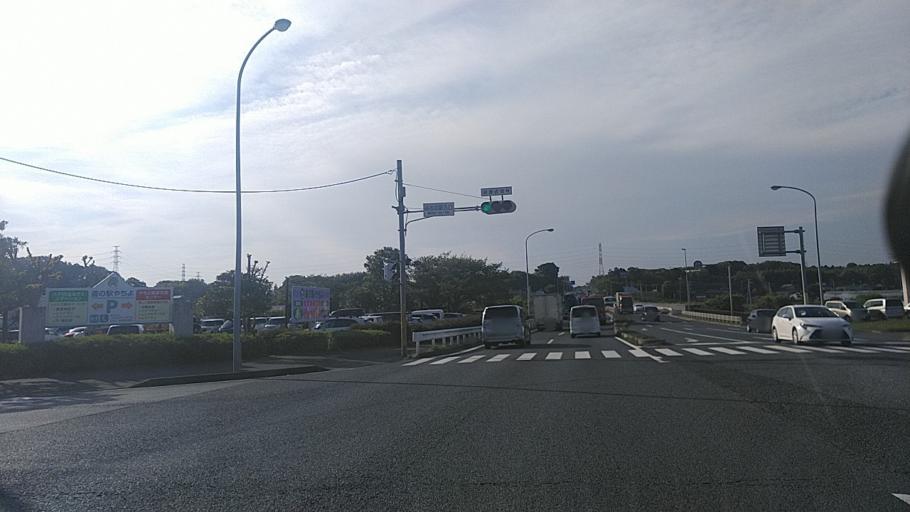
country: JP
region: Chiba
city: Shiroi
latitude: 35.7588
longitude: 140.1078
